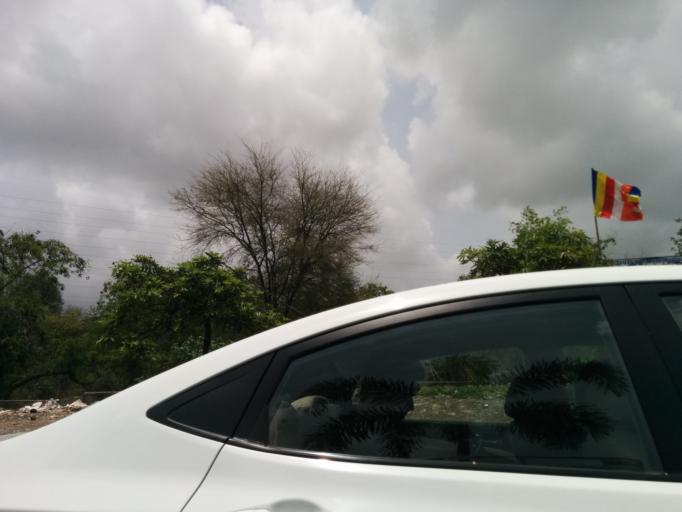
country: IN
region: Maharashtra
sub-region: Mumbai Suburban
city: Powai
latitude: 19.1370
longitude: 72.8732
